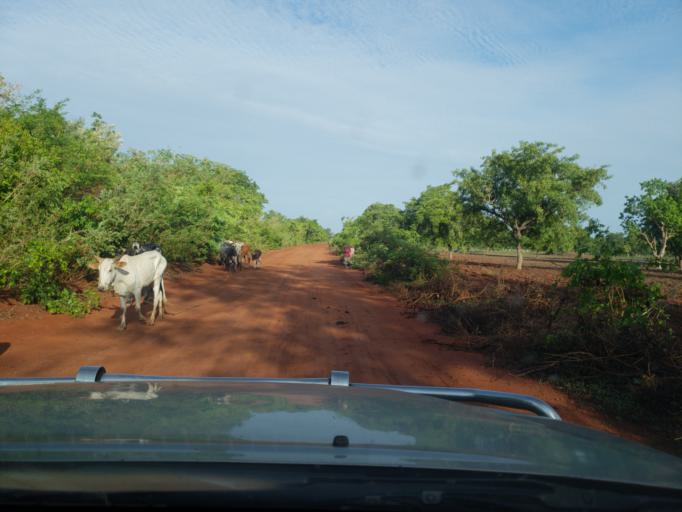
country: ML
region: Sikasso
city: Koutiala
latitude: 12.4246
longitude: -5.6589
